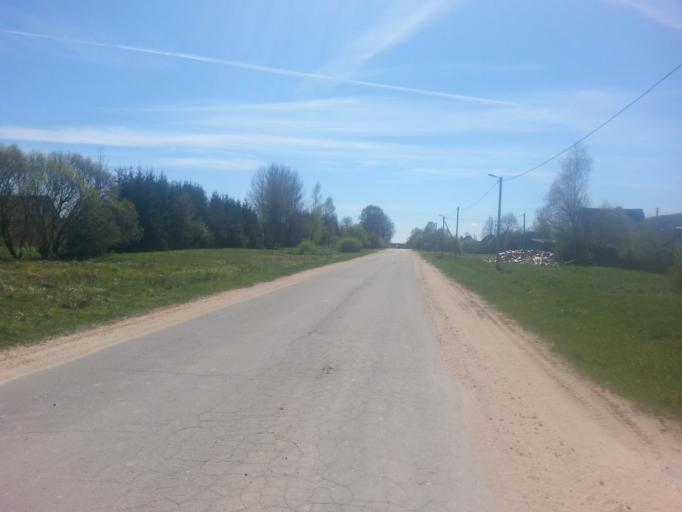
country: BY
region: Minsk
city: Narach
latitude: 54.9449
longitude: 26.6956
